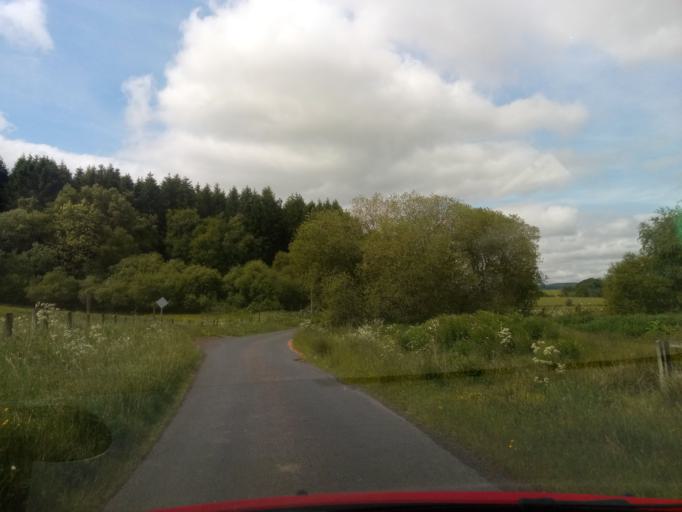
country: GB
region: Scotland
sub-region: The Scottish Borders
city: Selkirk
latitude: 55.5311
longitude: -2.8429
